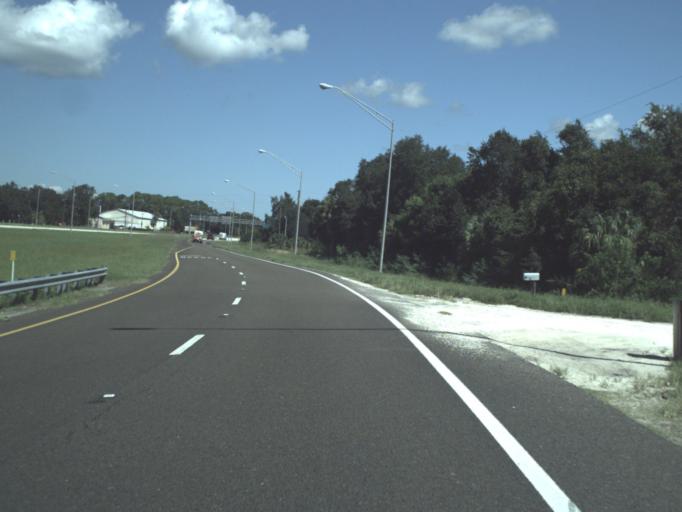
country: US
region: Florida
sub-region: Manatee County
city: Memphis
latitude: 27.5414
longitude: -82.5635
